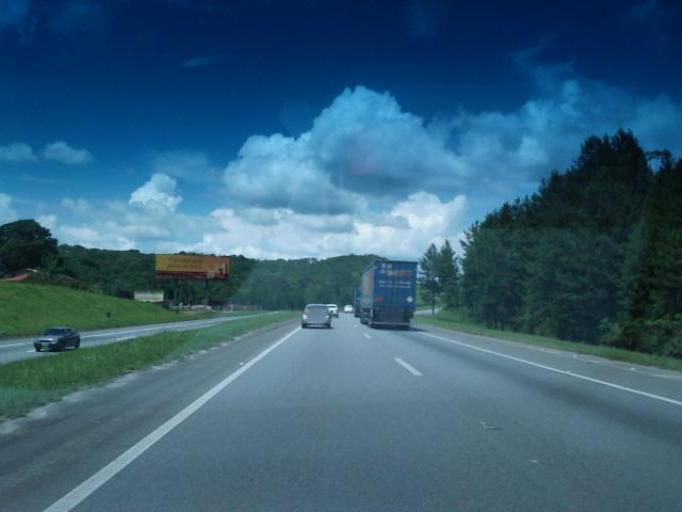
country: BR
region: Sao Paulo
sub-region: Juquitiba
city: Juquitiba
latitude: -23.9537
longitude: -47.1060
